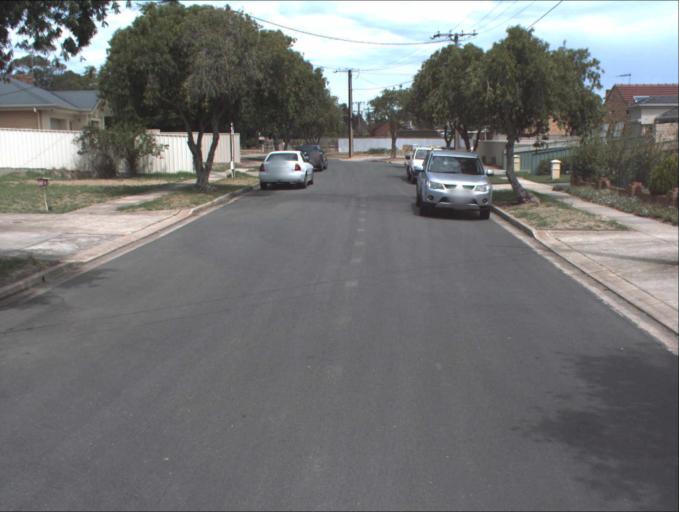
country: AU
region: South Australia
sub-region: Port Adelaide Enfield
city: Enfield
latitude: -34.8542
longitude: 138.6142
